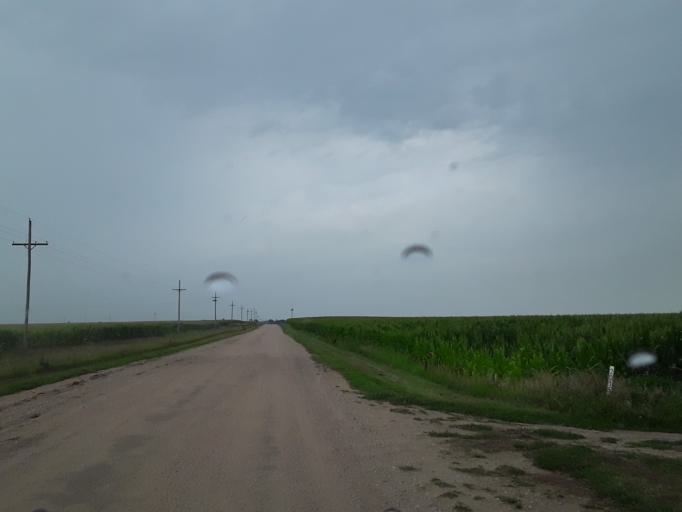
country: US
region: Nebraska
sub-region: Saunders County
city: Yutan
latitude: 41.1684
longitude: -96.4448
